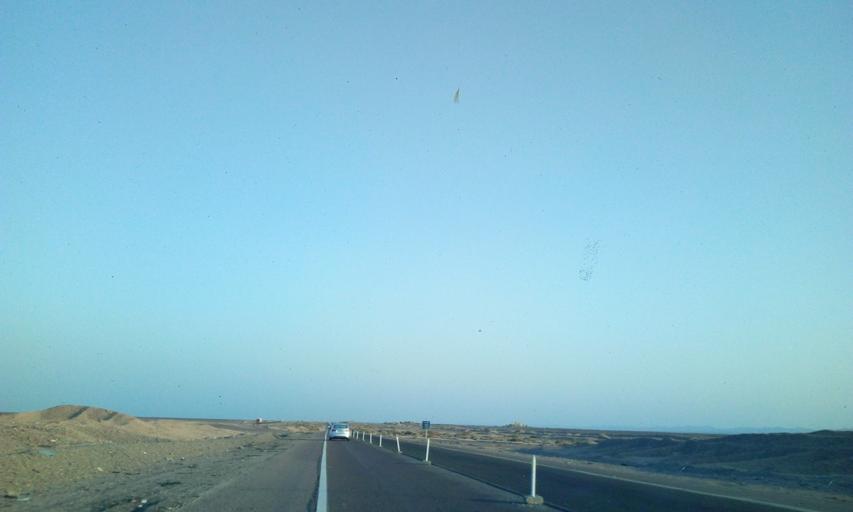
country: EG
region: South Sinai
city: Tor
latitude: 27.9046
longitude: 33.3994
